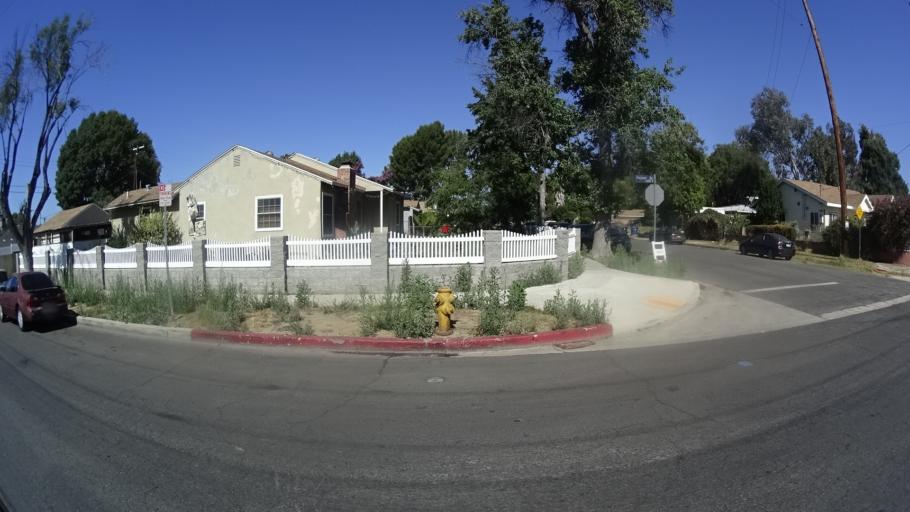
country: US
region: California
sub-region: Los Angeles County
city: Van Nuys
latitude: 34.1891
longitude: -118.4858
